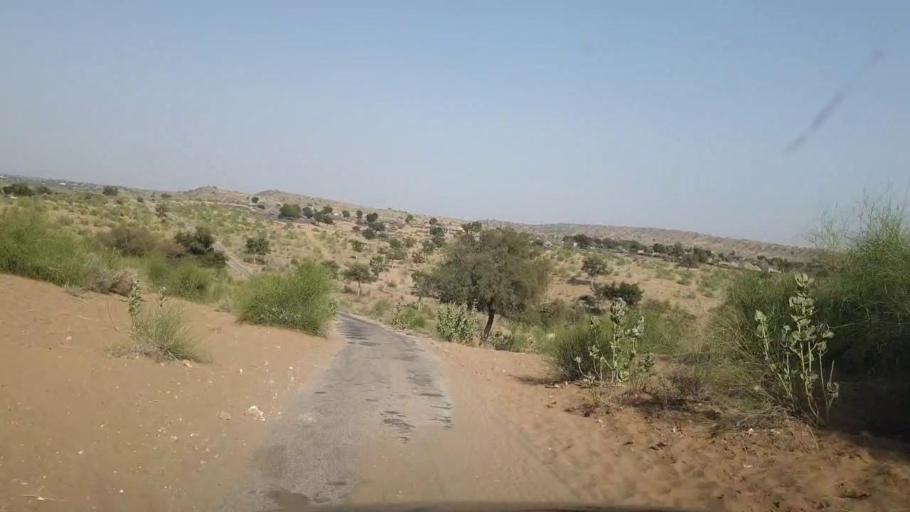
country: PK
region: Sindh
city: Islamkot
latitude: 25.1148
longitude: 70.4346
